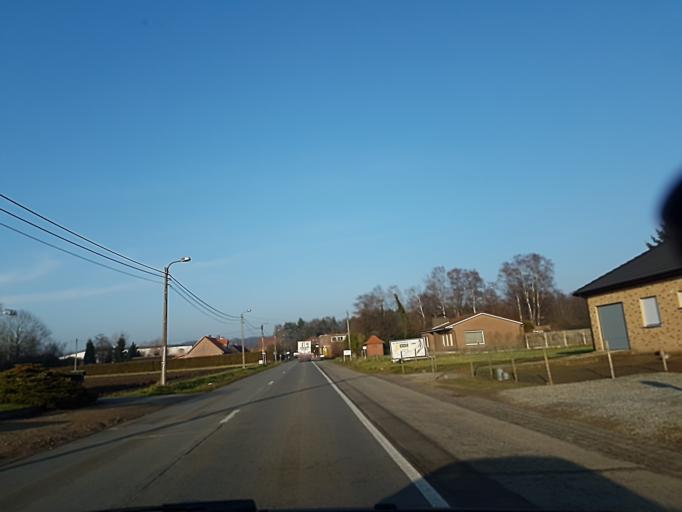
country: BE
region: Flanders
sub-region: Provincie Antwerpen
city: Heist-op-den-Berg
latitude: 51.0645
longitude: 4.7363
